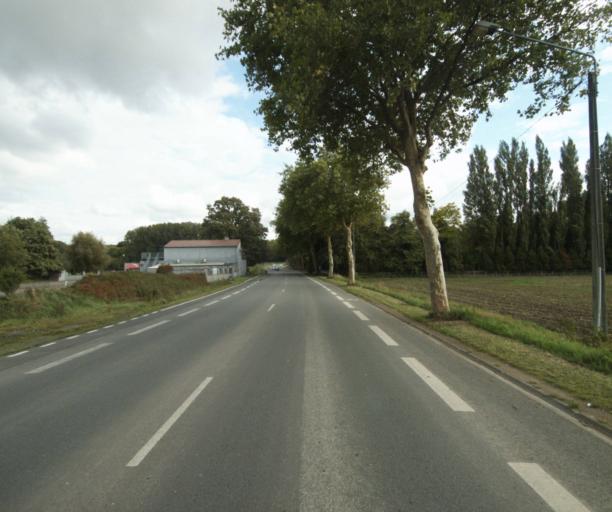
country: FR
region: Nord-Pas-de-Calais
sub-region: Departement du Nord
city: Premesques
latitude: 50.6534
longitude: 2.9380
